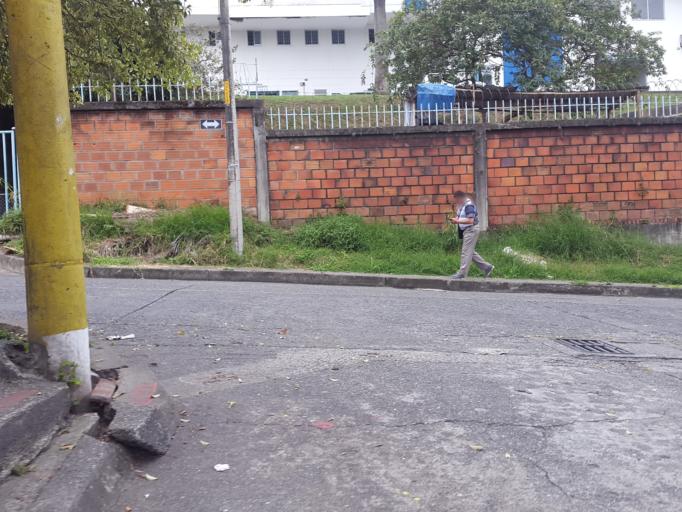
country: CO
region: Risaralda
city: Pereira
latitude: 4.8178
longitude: -75.7121
